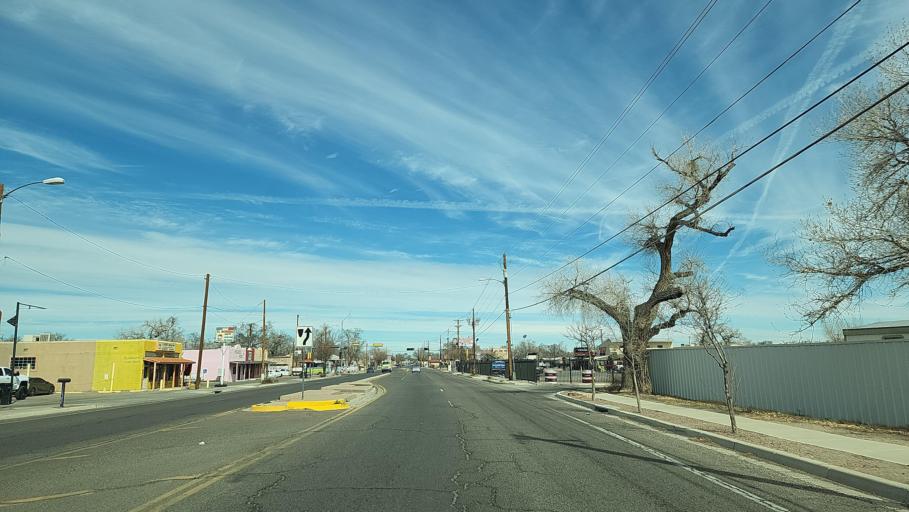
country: US
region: New Mexico
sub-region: Bernalillo County
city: South Valley
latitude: 35.0371
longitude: -106.6794
